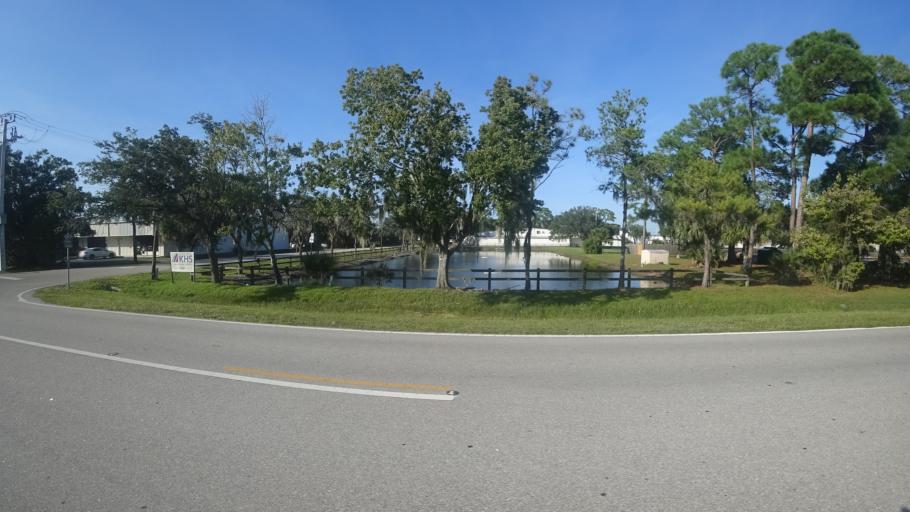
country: US
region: Florida
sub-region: Sarasota County
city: North Sarasota
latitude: 27.3817
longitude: -82.5344
